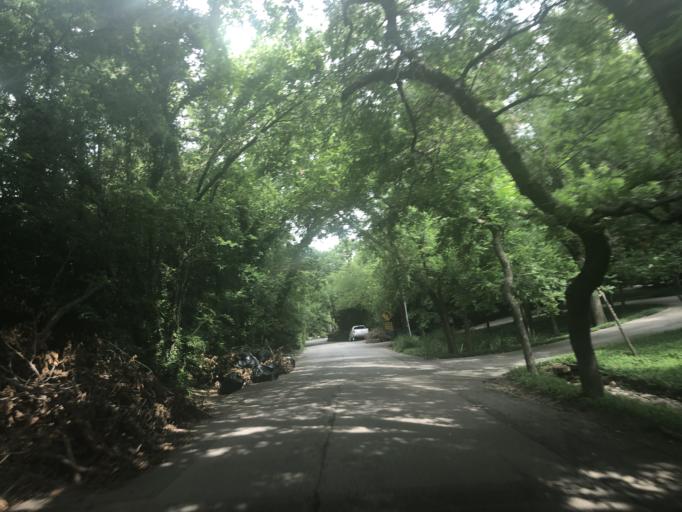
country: US
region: Texas
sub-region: Dallas County
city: University Park
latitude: 32.8606
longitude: -96.8329
